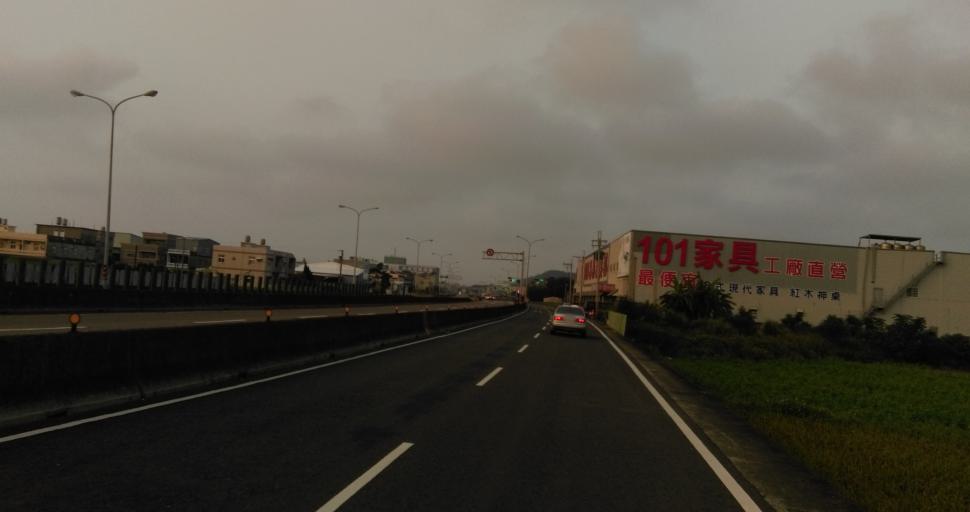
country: TW
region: Taiwan
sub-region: Hsinchu
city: Zhubei
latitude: 24.8649
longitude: 120.9529
